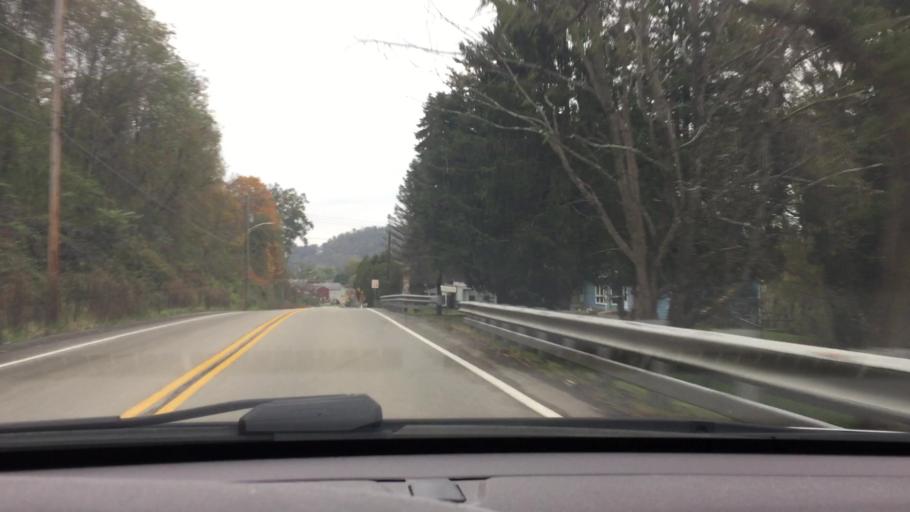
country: US
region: Pennsylvania
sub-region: Fayette County
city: Fairhope
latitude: 40.0927
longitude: -79.8451
